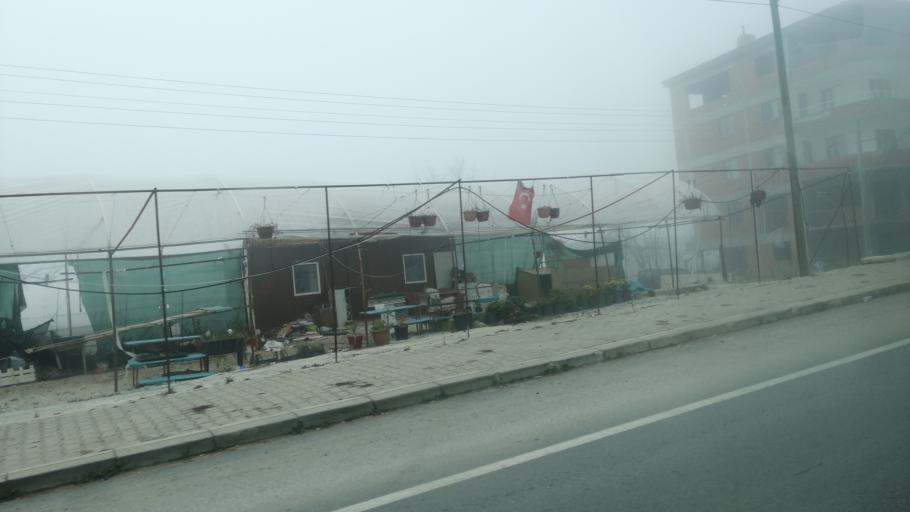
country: TR
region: Yalova
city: Korukoy
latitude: 40.6521
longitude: 29.1831
